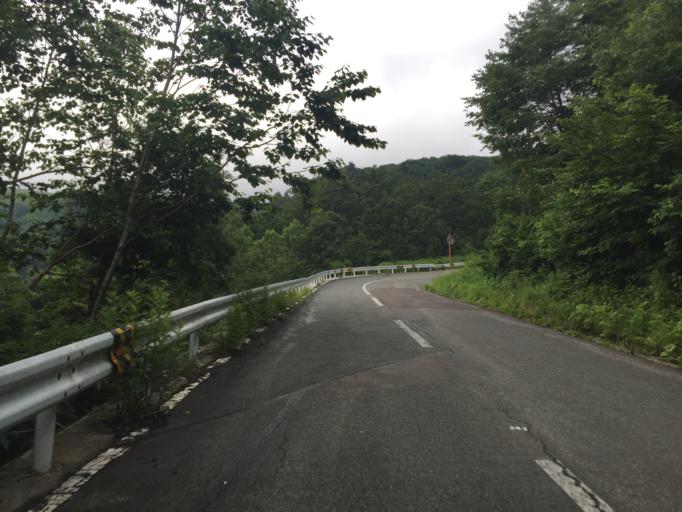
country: JP
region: Yamagata
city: Yonezawa
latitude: 37.7560
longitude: 140.1041
